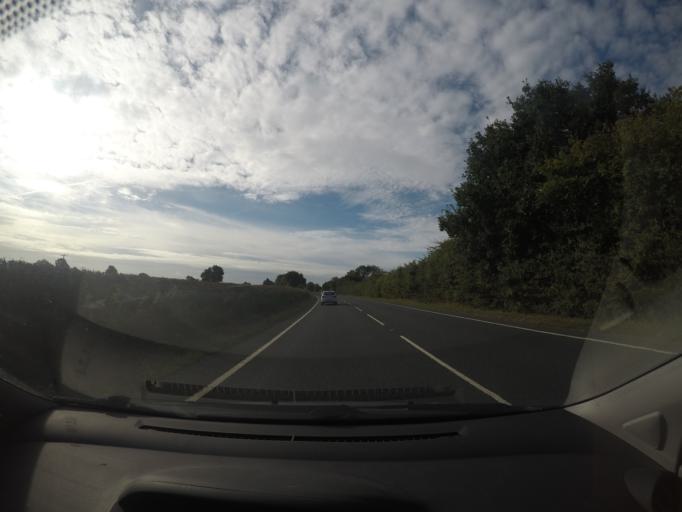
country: GB
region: England
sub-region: North Yorkshire
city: Riccall
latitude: 53.8415
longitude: -1.0559
